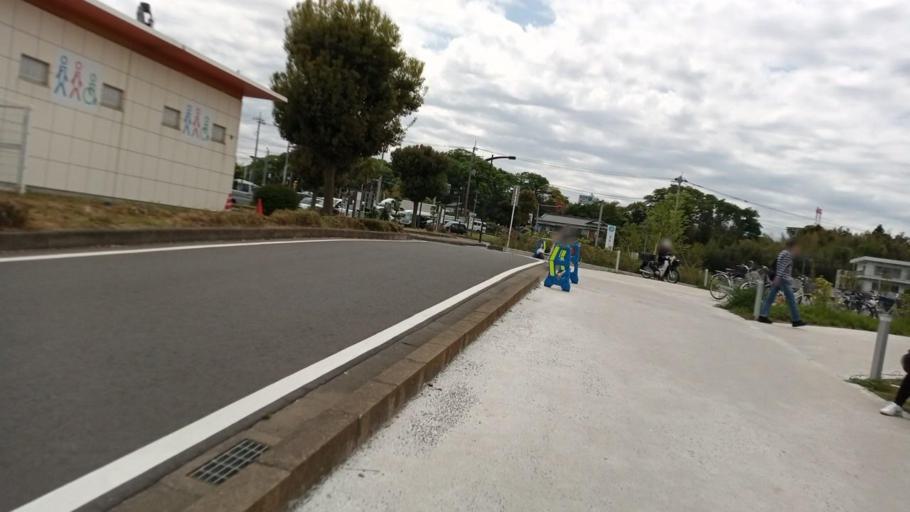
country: JP
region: Chiba
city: Abiko
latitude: 35.8576
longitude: 140.0231
